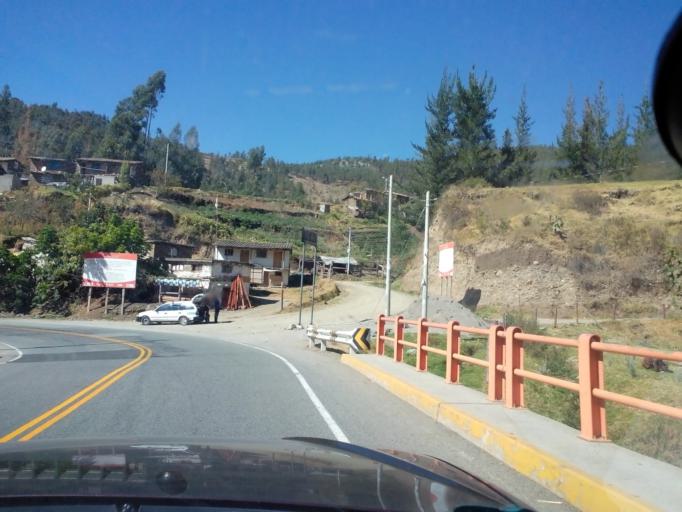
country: PE
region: Apurimac
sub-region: Provincia de Abancay
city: Cachora
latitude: -13.5570
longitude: -72.7669
